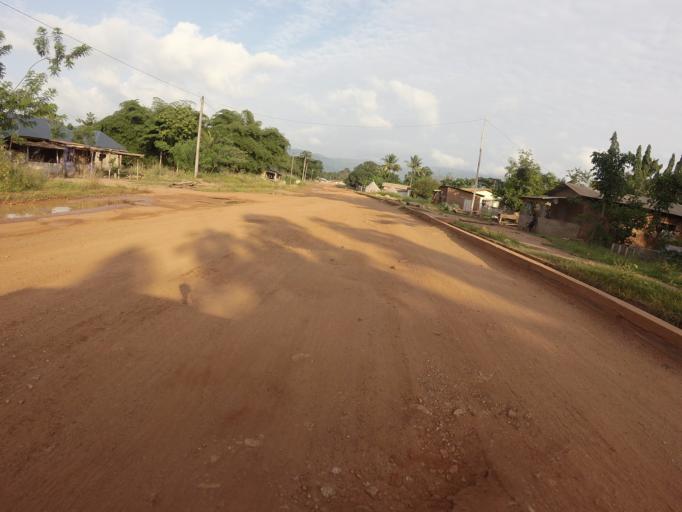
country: GH
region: Volta
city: Kpandu
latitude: 6.9657
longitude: 0.4568
